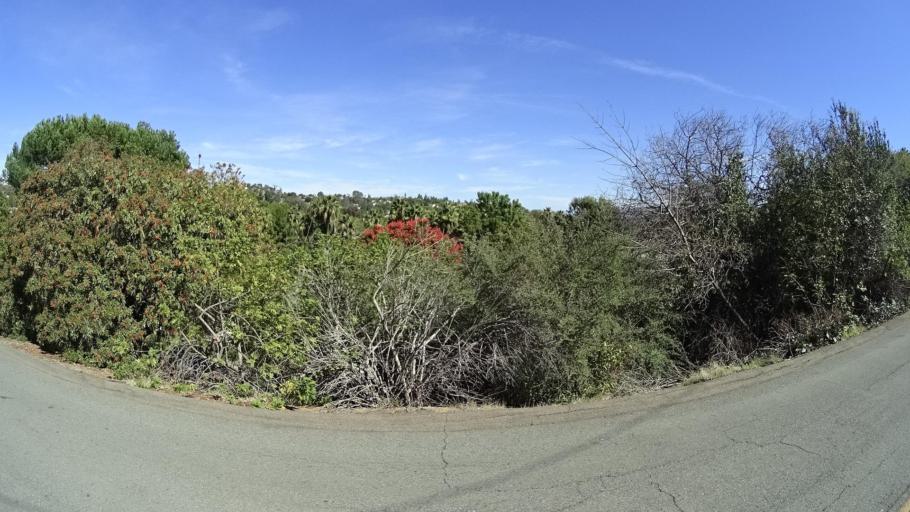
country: US
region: California
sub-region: San Diego County
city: Casa de Oro-Mount Helix
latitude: 32.7496
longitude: -116.9663
